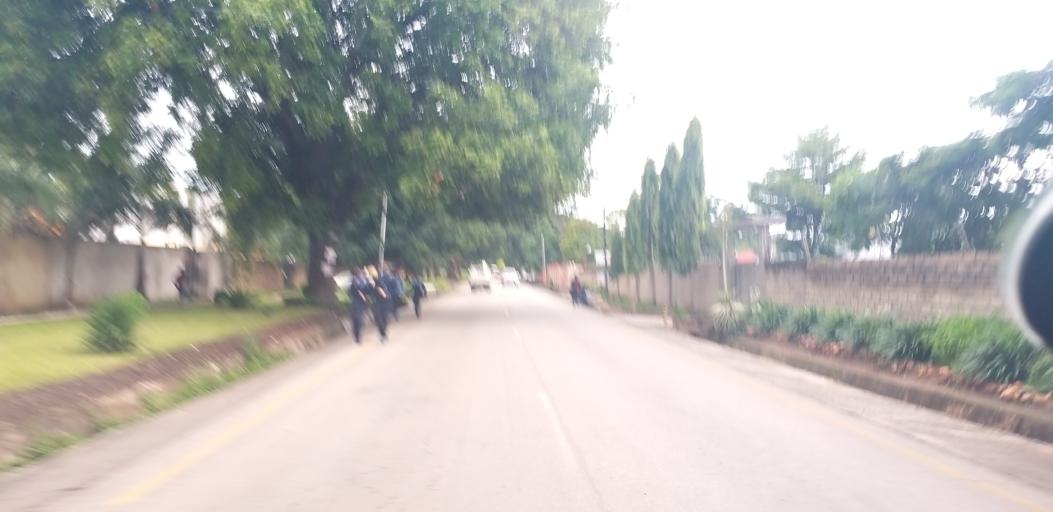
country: ZM
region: Lusaka
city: Lusaka
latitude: -15.4204
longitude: 28.2969
